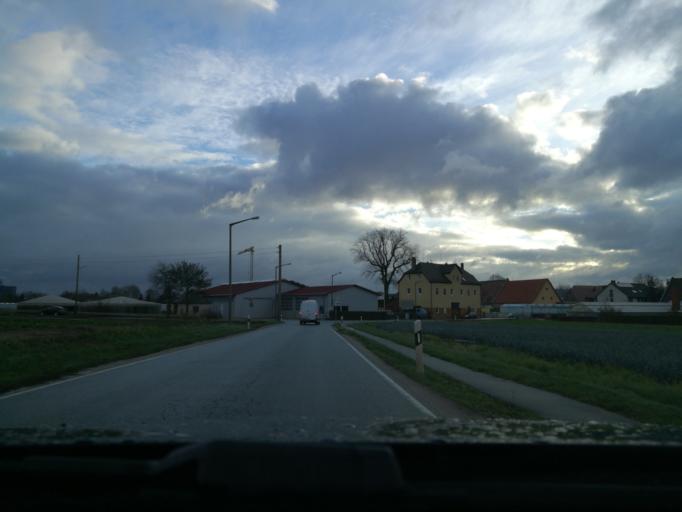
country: DE
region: Bavaria
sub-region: Regierungsbezirk Mittelfranken
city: Wetzendorf
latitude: 49.4726
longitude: 11.0346
